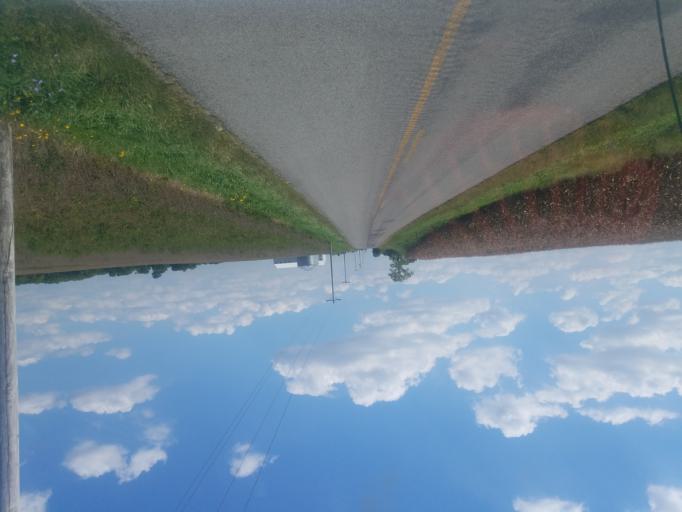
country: US
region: Ohio
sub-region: Hardin County
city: Ada
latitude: 40.6525
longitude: -83.8692
